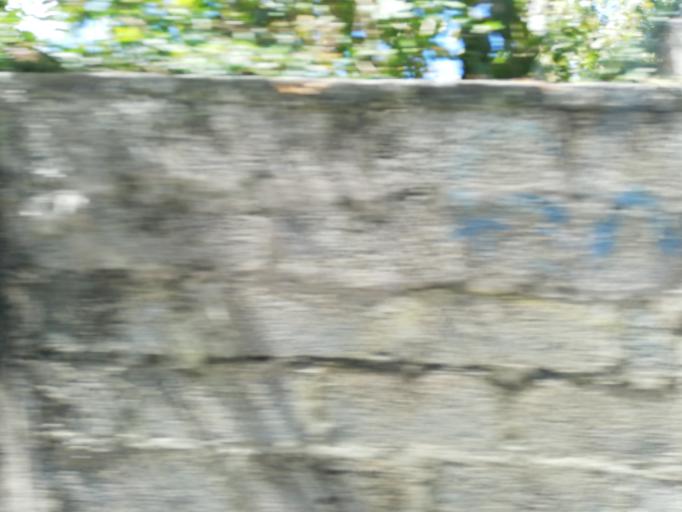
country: MU
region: Plaines Wilhems
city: Ebene
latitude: -20.2345
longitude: 57.4699
